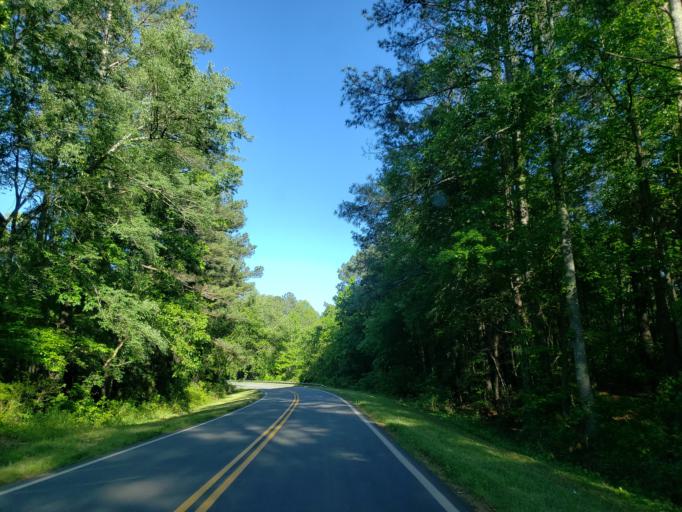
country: US
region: Georgia
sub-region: Haralson County
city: Tallapoosa
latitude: 33.7943
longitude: -85.2653
